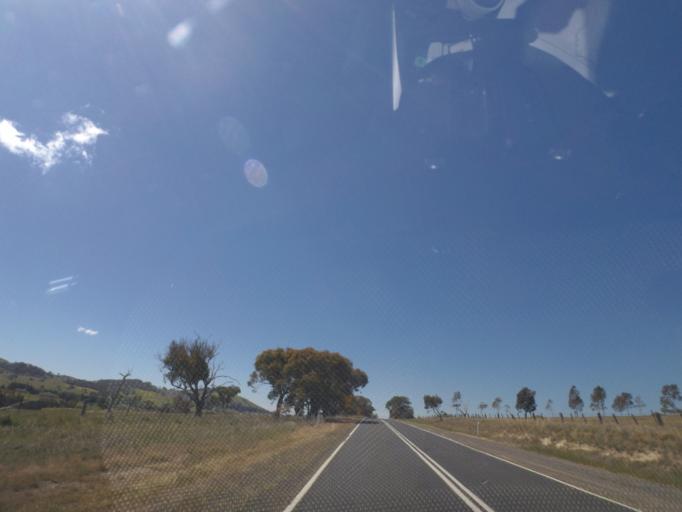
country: AU
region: Victoria
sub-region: Hume
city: Sunbury
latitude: -37.0831
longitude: 144.7614
